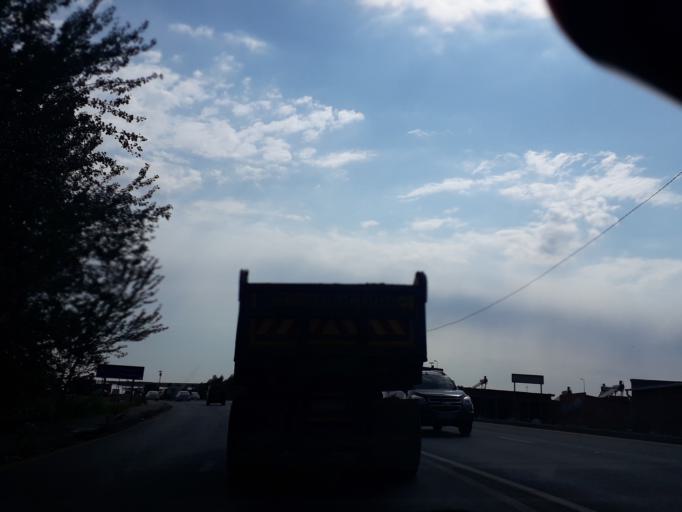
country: ZA
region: Gauteng
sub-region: City of Johannesburg Metropolitan Municipality
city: Modderfontein
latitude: -26.1059
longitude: 28.1224
